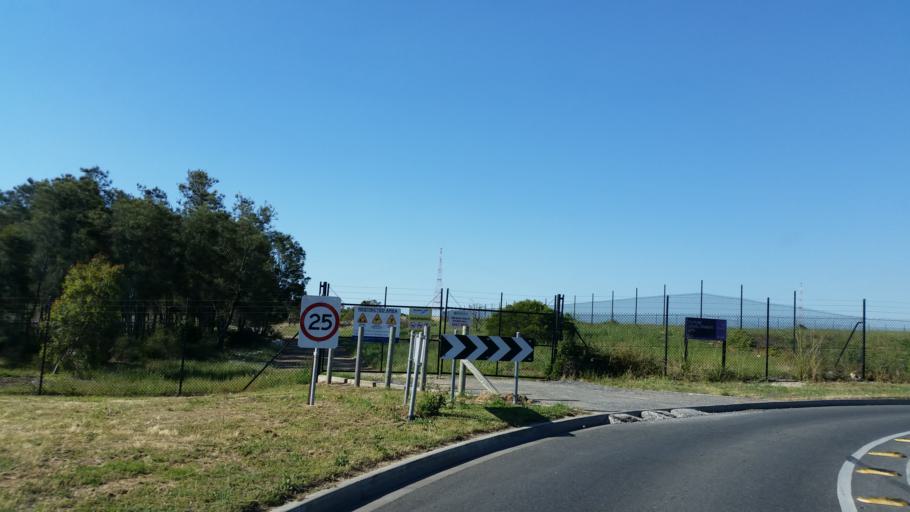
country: AU
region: South Australia
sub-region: Port Adelaide Enfield
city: Birkenhead
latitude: -34.8144
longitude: 138.5082
